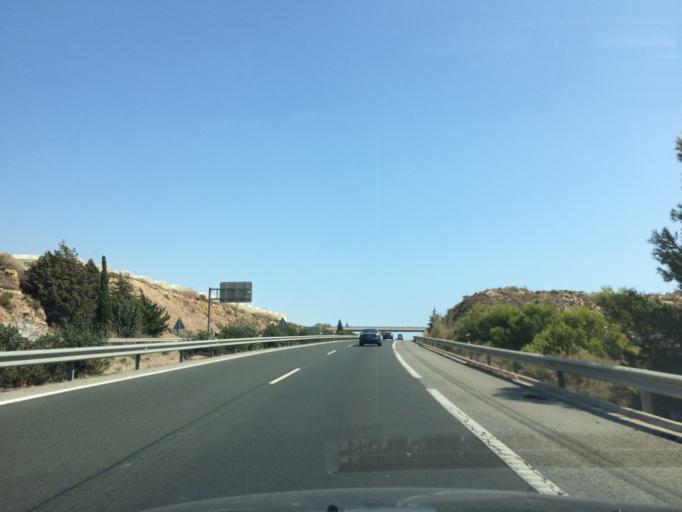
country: ES
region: Andalusia
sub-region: Provincia de Almeria
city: Adra
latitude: 36.7690
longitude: -2.9794
